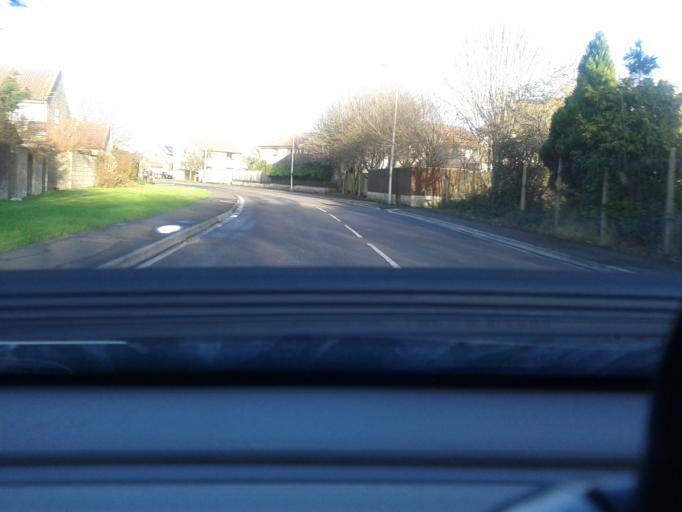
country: GB
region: England
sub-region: North Somerset
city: St. Georges
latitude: 51.3652
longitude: -2.9104
